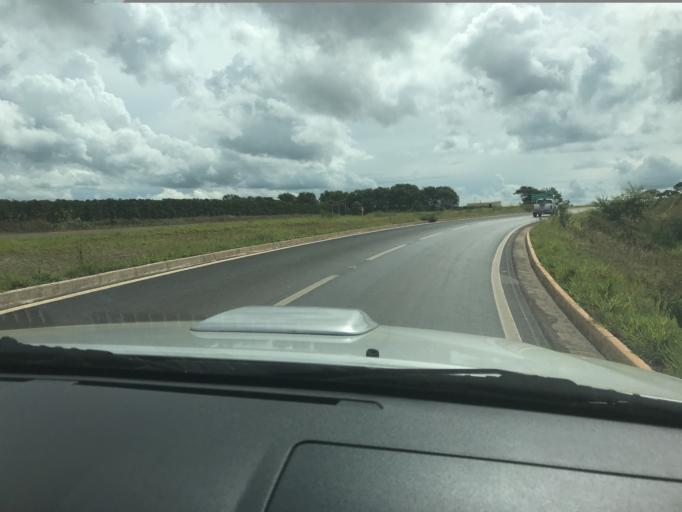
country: BR
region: Minas Gerais
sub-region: Patrocinio
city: Patrocinio
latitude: -19.0962
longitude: -46.6679
